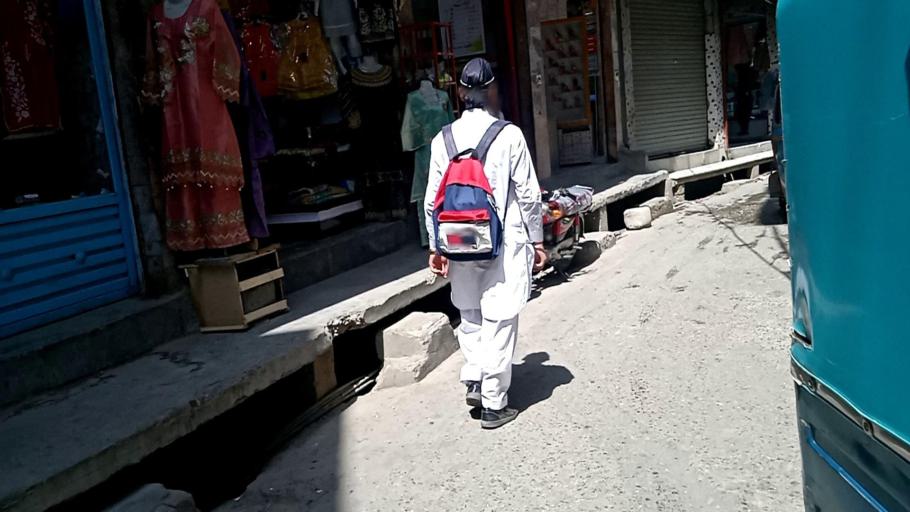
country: PK
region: Khyber Pakhtunkhwa
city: Mingora
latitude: 34.7763
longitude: 72.3531
